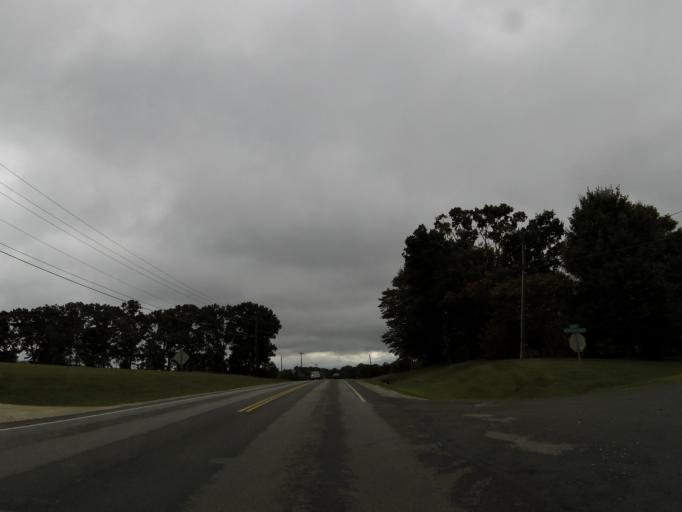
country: US
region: Tennessee
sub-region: Hamilton County
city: Collegedale
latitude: 35.1270
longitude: -85.0444
